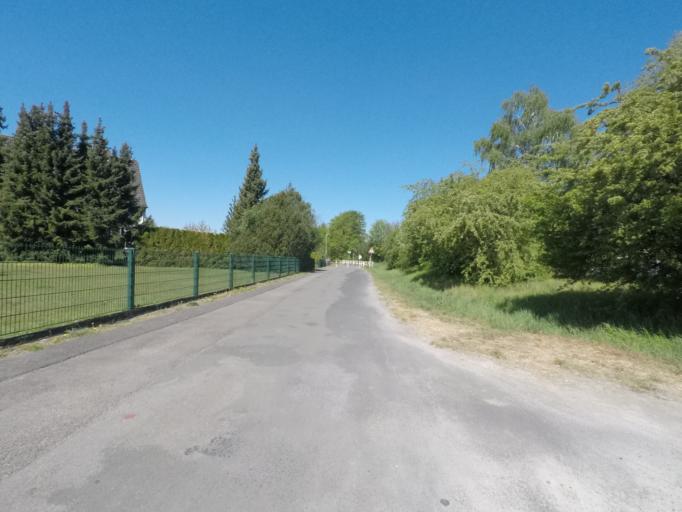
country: DE
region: North Rhine-Westphalia
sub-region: Regierungsbezirk Detmold
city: Bielefeld
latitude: 52.0178
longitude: 8.5712
